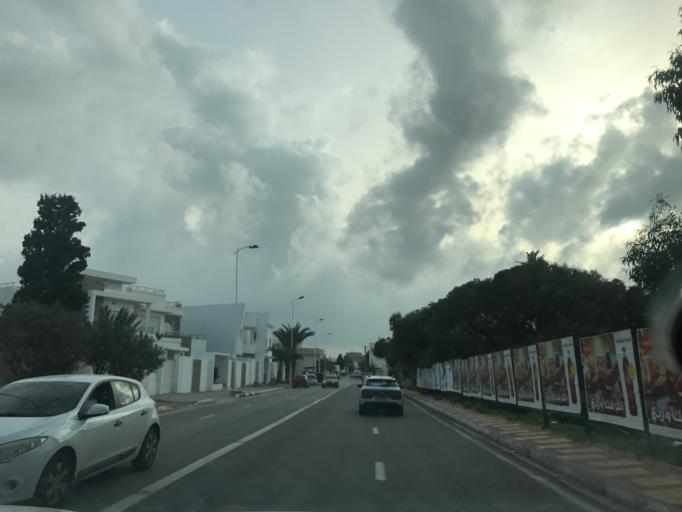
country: TN
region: Al Munastir
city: Saqanis
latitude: 35.7789
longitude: 10.7988
